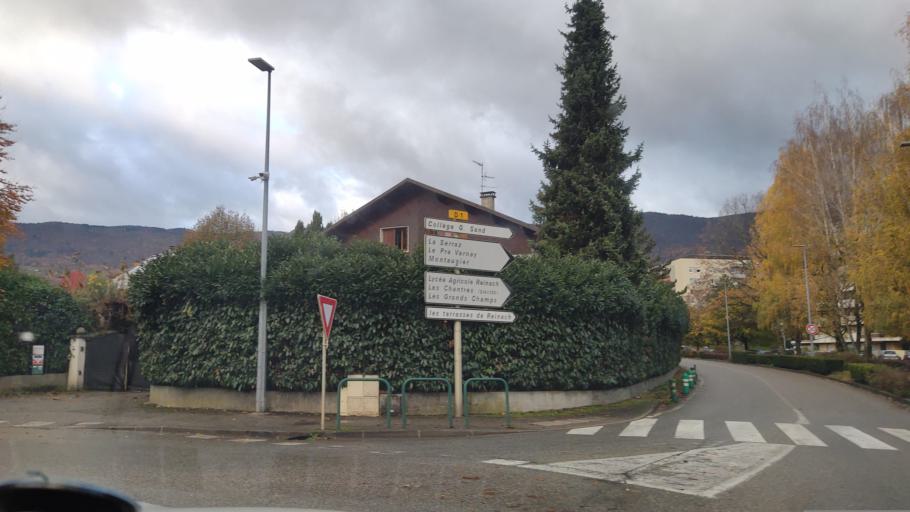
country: FR
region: Rhone-Alpes
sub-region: Departement de la Savoie
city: La Motte-Servolex
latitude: 45.5932
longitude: 5.8743
